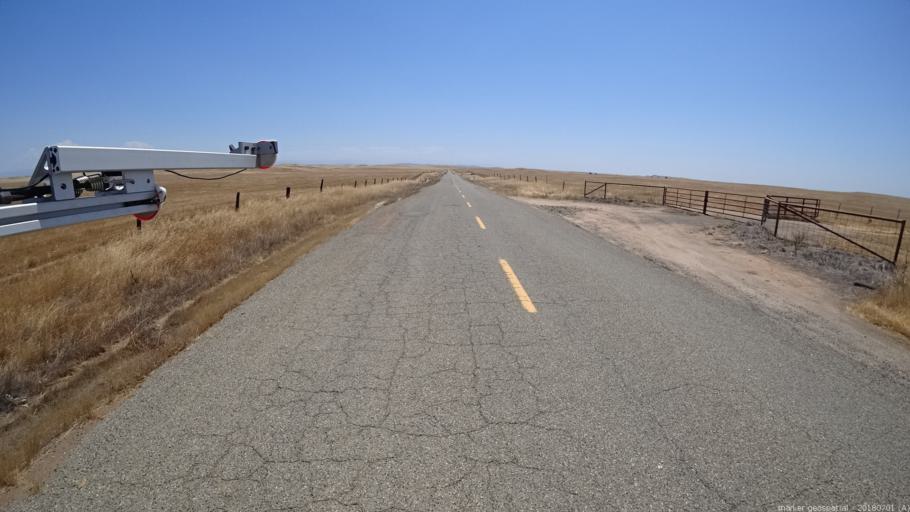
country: US
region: California
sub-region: Madera County
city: Madera Acres
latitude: 37.1193
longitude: -120.0111
